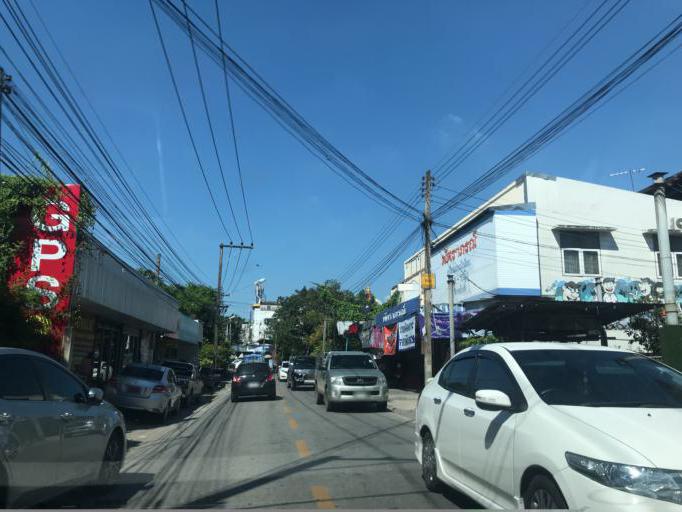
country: TH
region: Chiang Mai
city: Chiang Mai
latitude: 18.7979
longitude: 98.9901
